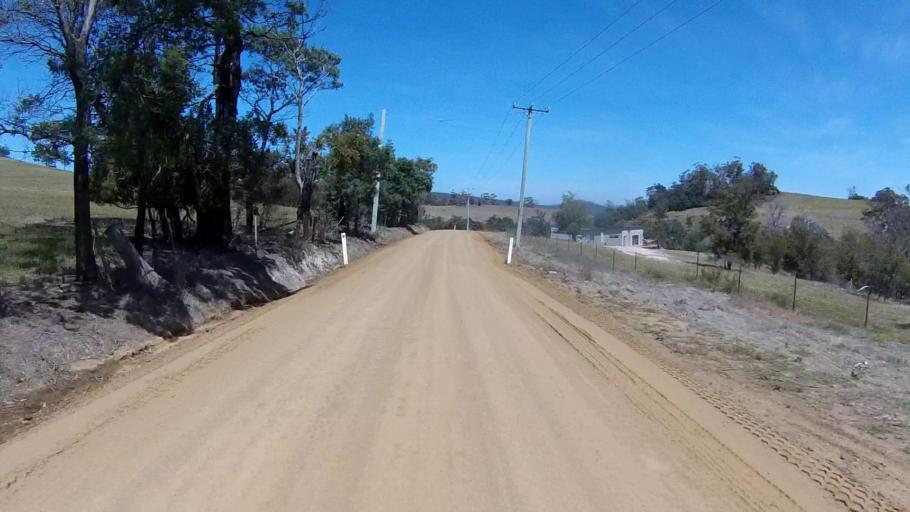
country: AU
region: Tasmania
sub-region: Sorell
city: Sorell
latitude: -42.7794
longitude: 147.6510
